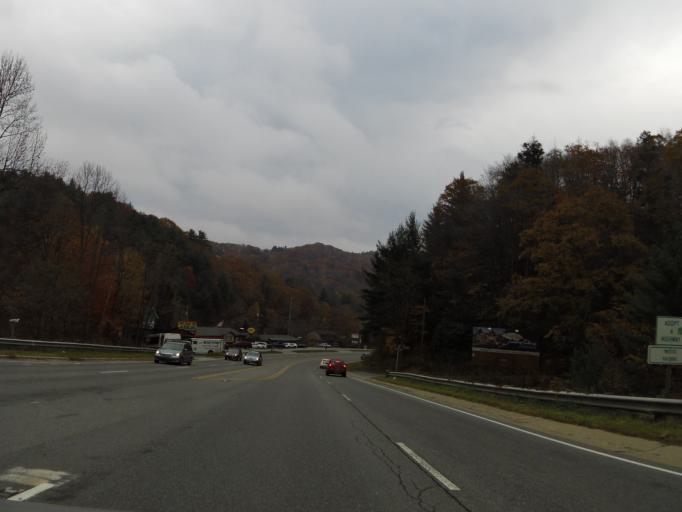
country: US
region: North Carolina
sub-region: Watauga County
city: Boone
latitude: 36.1815
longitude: -81.6492
